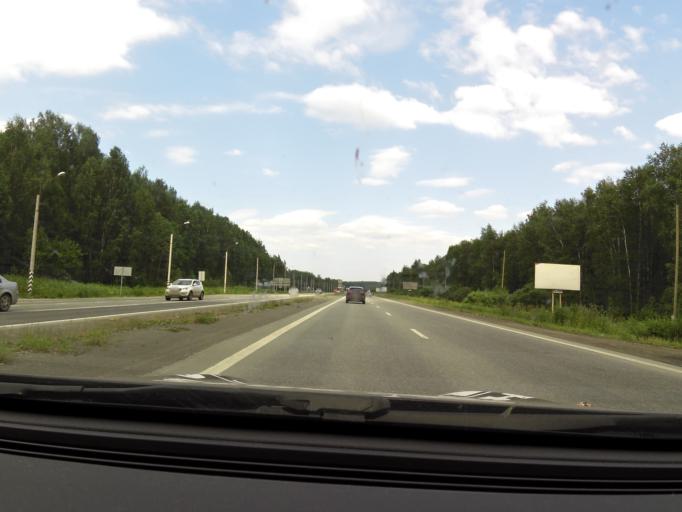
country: RU
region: Sverdlovsk
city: Severka
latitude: 56.8425
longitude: 60.2001
